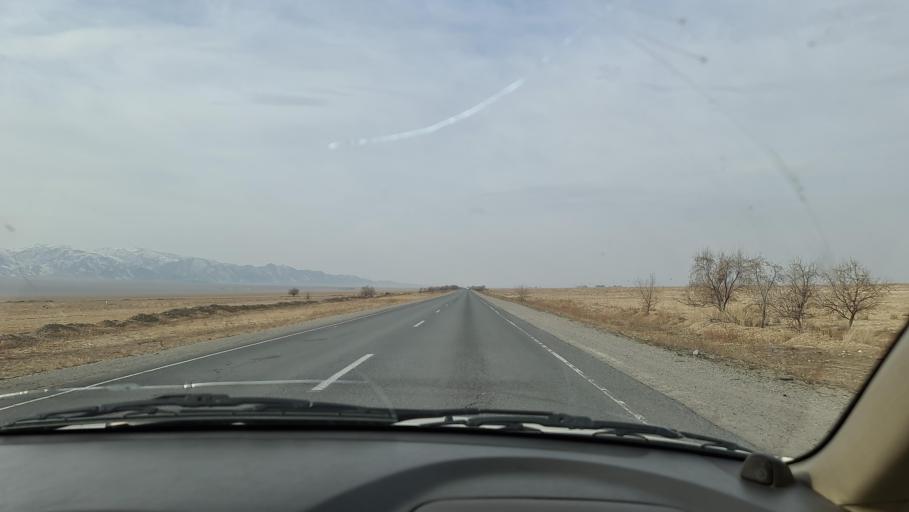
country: KG
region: Chuy
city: Tokmok
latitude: 43.3570
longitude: 75.4161
